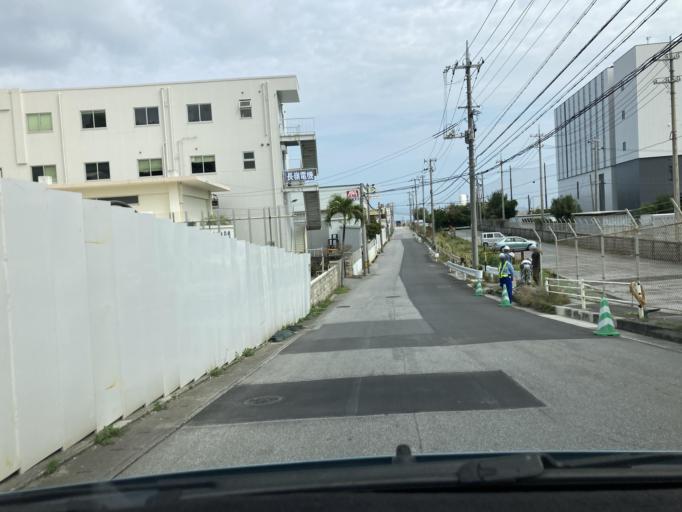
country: JP
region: Okinawa
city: Ginowan
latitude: 26.2701
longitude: 127.7153
